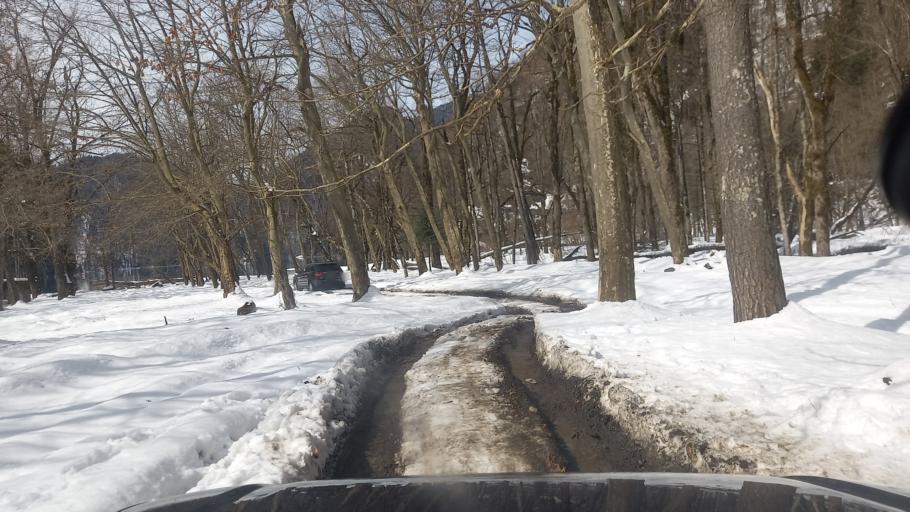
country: GE
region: Abkhazia
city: Gagra
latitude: 43.4814
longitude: 40.5612
